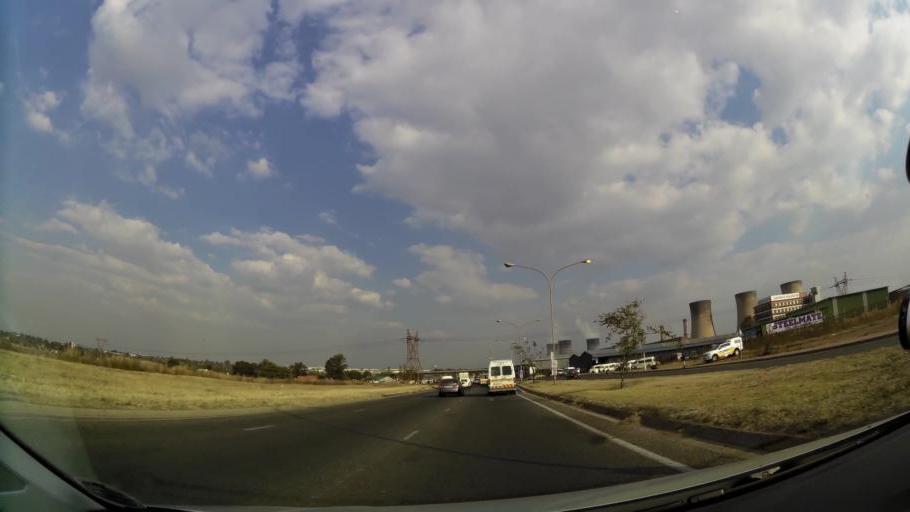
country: ZA
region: Gauteng
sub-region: City of Johannesburg Metropolitan Municipality
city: Modderfontein
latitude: -26.1071
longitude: 28.1967
